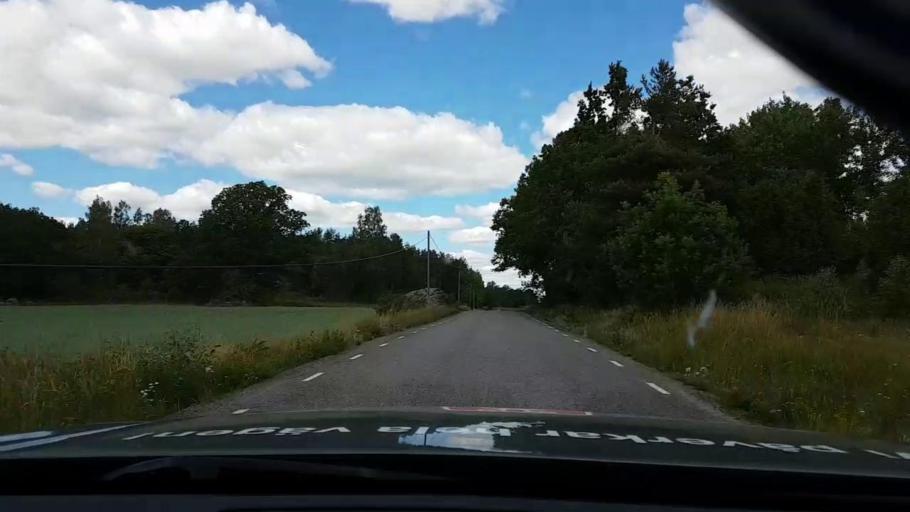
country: SE
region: Kalmar
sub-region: Vasterviks Kommun
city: Forserum
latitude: 57.9942
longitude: 16.5999
